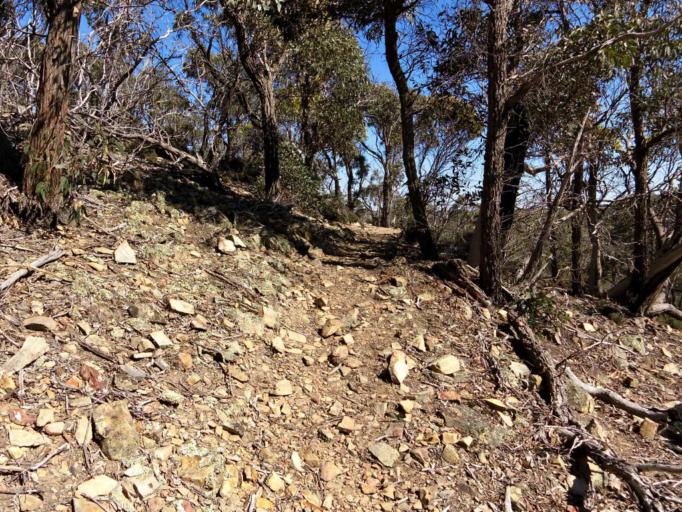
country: AU
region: Victoria
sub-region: Moorabool
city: Bacchus Marsh
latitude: -37.6677
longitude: 144.3203
